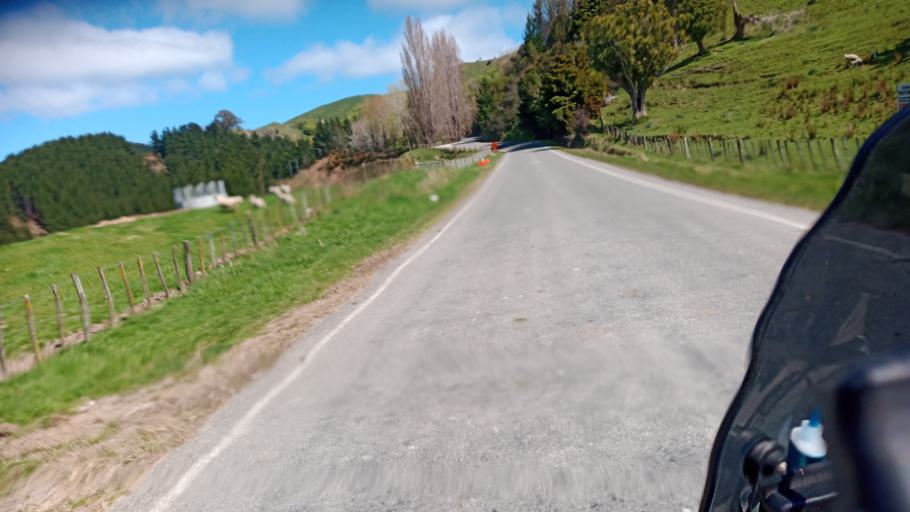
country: NZ
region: Gisborne
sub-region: Gisborne District
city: Gisborne
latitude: -38.7887
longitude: 177.7825
